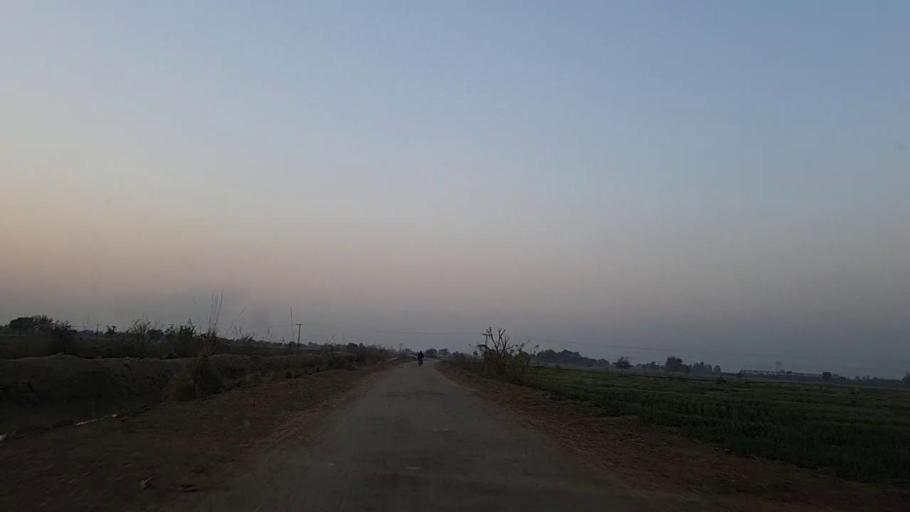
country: PK
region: Sindh
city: Hala
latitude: 25.9467
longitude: 68.4301
